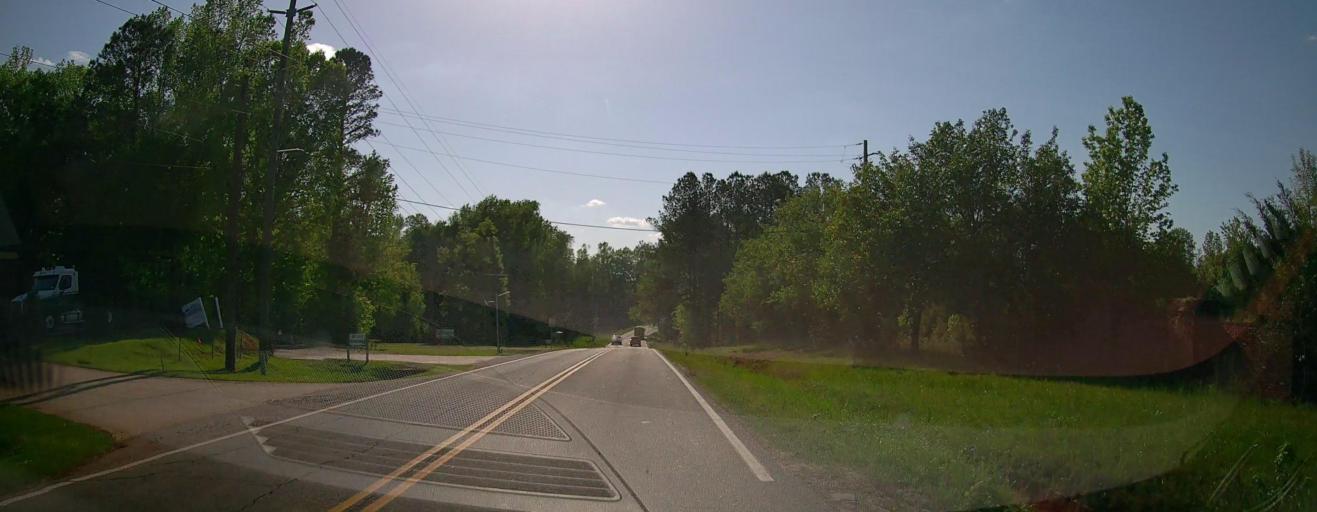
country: US
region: Georgia
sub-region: Morgan County
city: Madison
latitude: 33.5639
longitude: -83.4865
